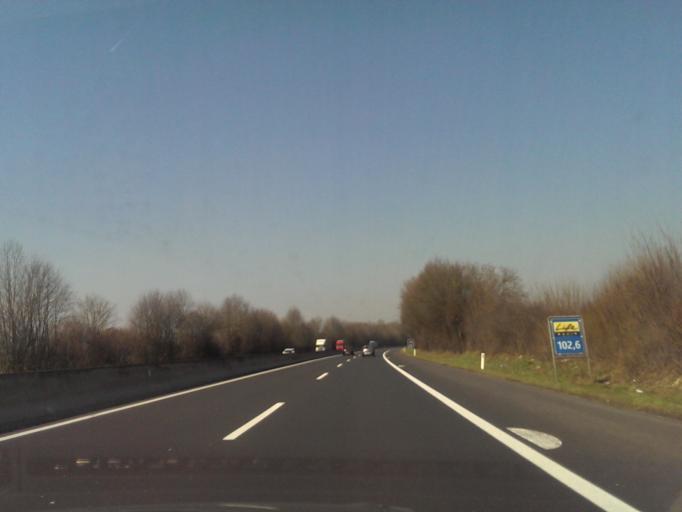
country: AT
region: Upper Austria
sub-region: Politischer Bezirk Scharding
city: Sankt Marienkirchen bei Schaerding
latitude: 48.3318
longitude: 13.4090
